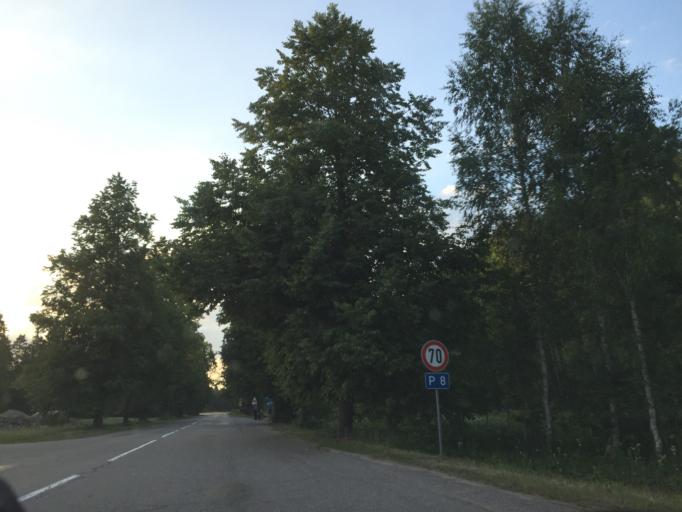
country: LV
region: Sigulda
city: Sigulda
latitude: 57.1082
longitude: 24.9246
